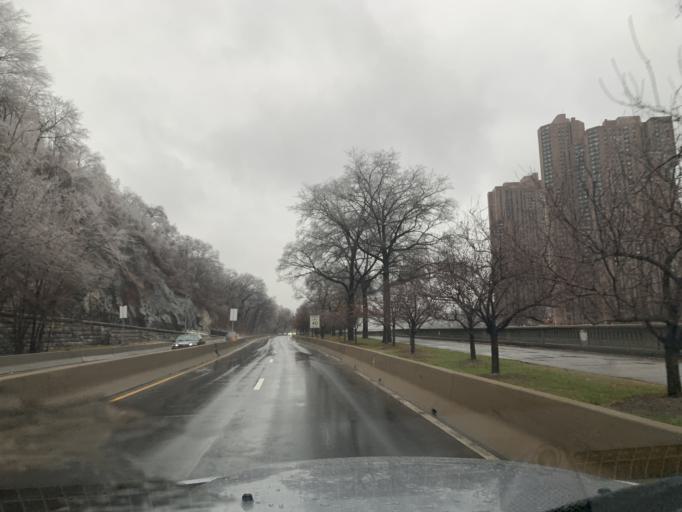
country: US
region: New York
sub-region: New York County
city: Inwood
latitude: 40.8497
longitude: -73.9268
